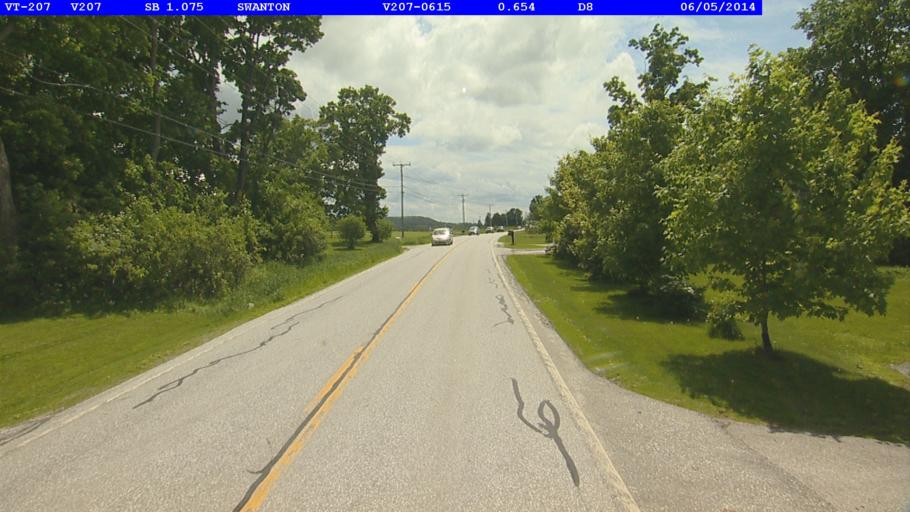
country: US
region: Vermont
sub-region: Franklin County
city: Saint Albans
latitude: 44.8546
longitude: -73.0752
